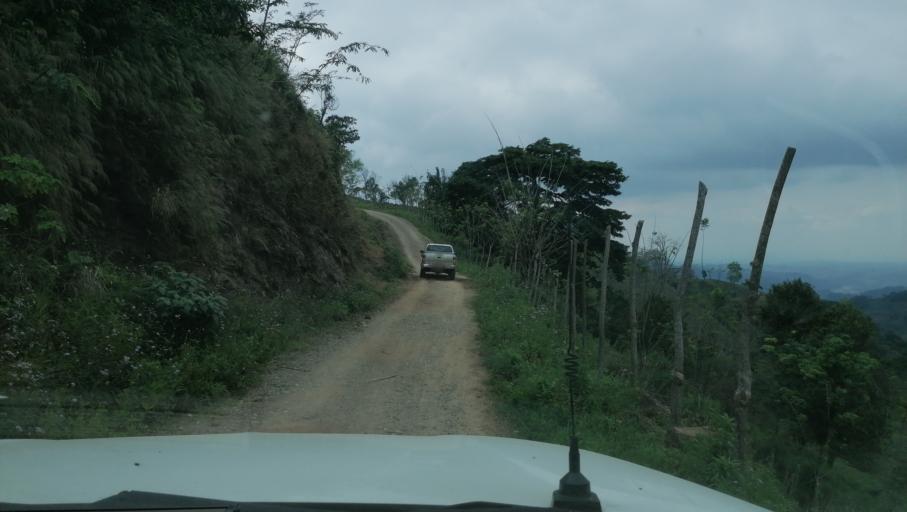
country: MX
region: Chiapas
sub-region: Francisco Leon
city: San Miguel la Sardina
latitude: 17.3450
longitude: -93.3103
